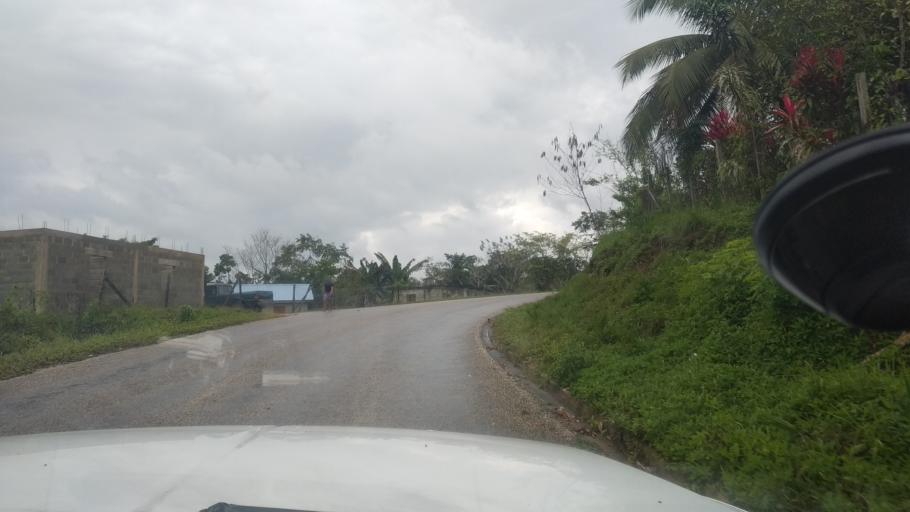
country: GT
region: Peten
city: San Luis
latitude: 16.2049
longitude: -89.1428
